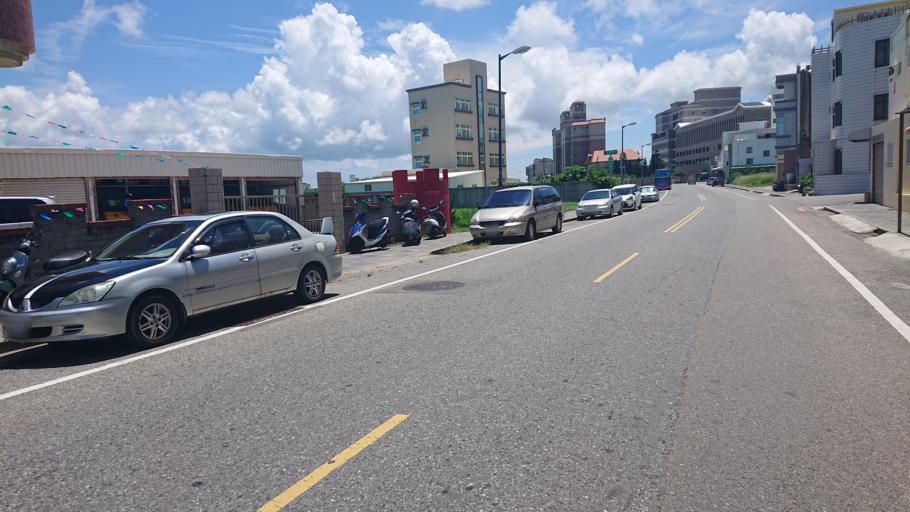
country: TW
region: Taiwan
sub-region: Penghu
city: Ma-kung
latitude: 23.5759
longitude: 119.5788
